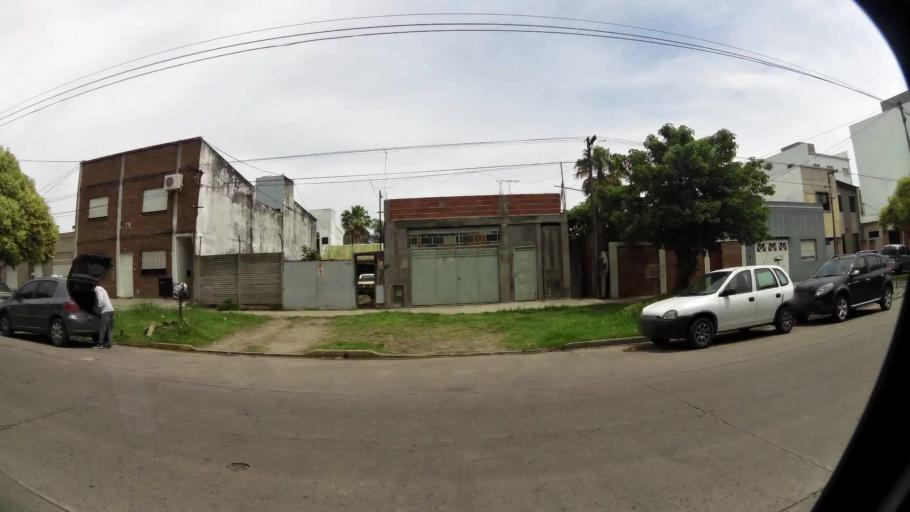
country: AR
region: Buenos Aires
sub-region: Partido de La Plata
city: La Plata
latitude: -34.9476
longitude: -57.9469
